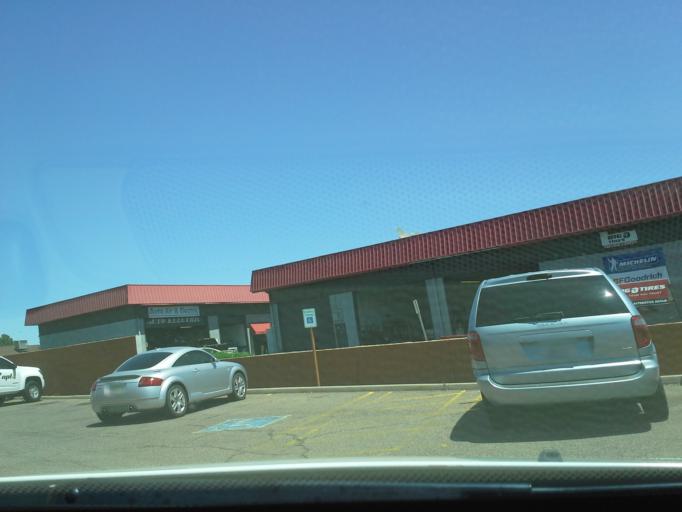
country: US
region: Arizona
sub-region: Maricopa County
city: Glendale
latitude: 33.6403
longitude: -112.1087
